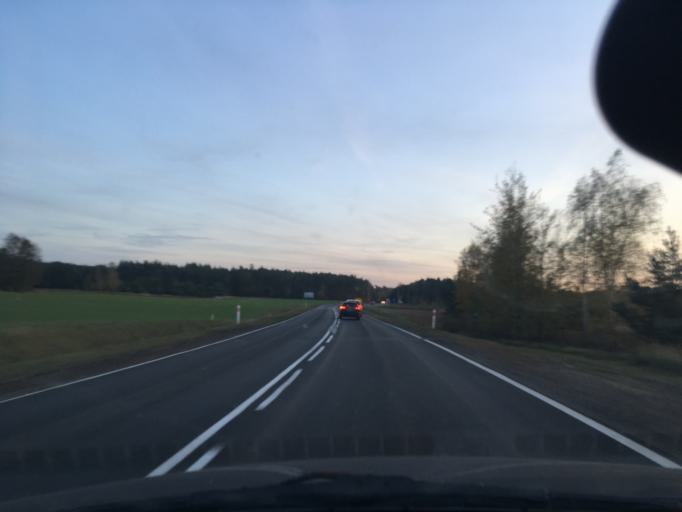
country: PL
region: Masovian Voivodeship
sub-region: Powiat plocki
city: Wyszogrod
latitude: 52.3518
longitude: 20.2090
